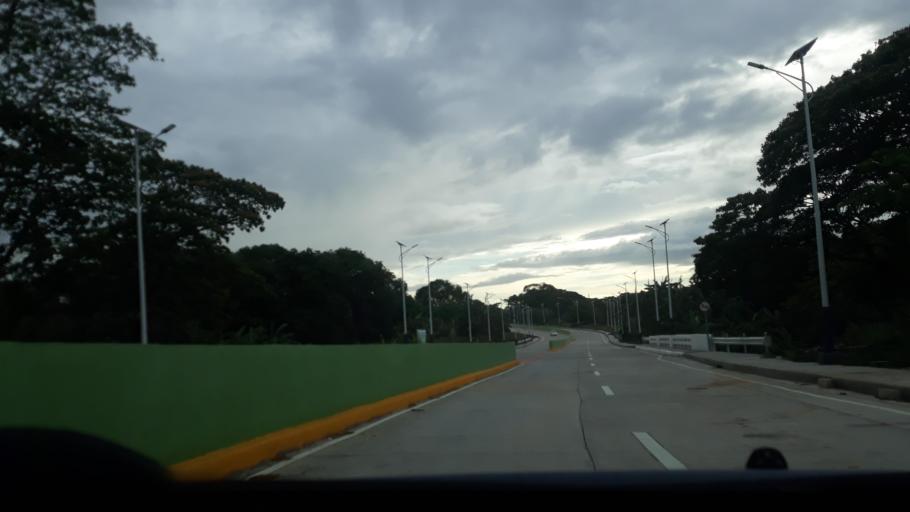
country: PH
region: Calabarzon
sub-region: Province of Cavite
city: Biga
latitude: 14.2883
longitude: 120.9637
